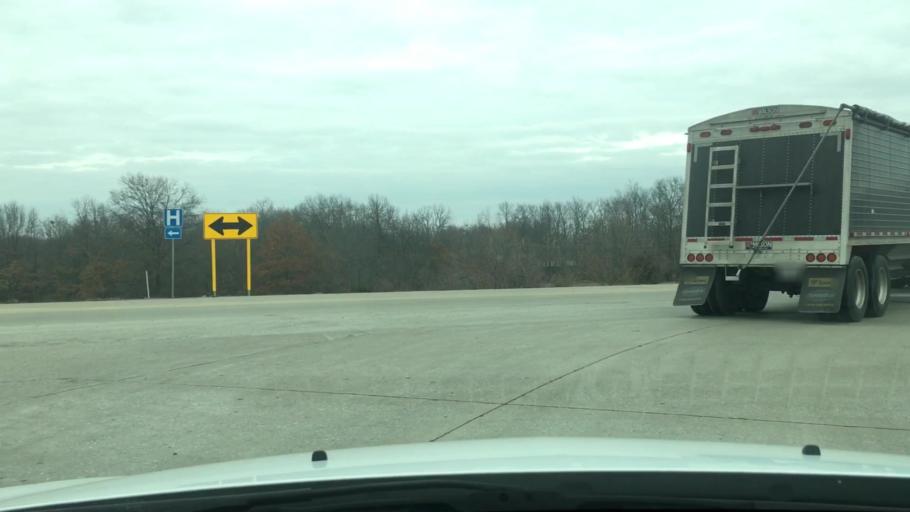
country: US
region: Missouri
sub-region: Audrain County
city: Mexico
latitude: 39.1624
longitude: -91.8406
